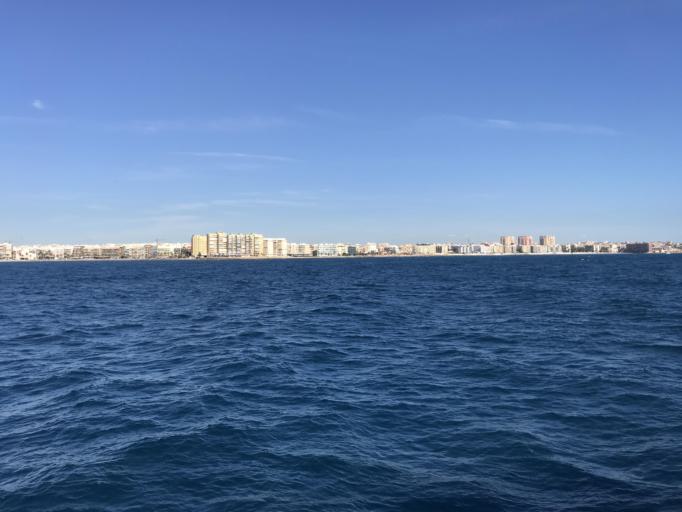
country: ES
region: Valencia
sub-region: Provincia de Alicante
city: Torrevieja
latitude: 37.9692
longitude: -0.6617
